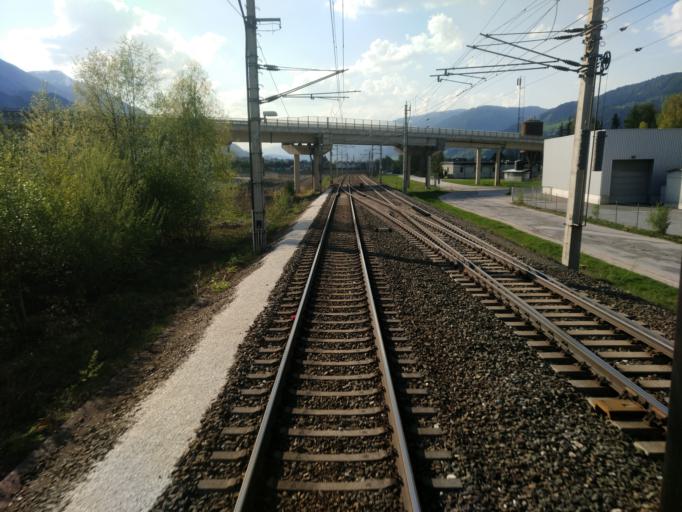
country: AT
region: Styria
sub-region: Politischer Bezirk Liezen
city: Trieben
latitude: 47.4909
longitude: 14.4845
